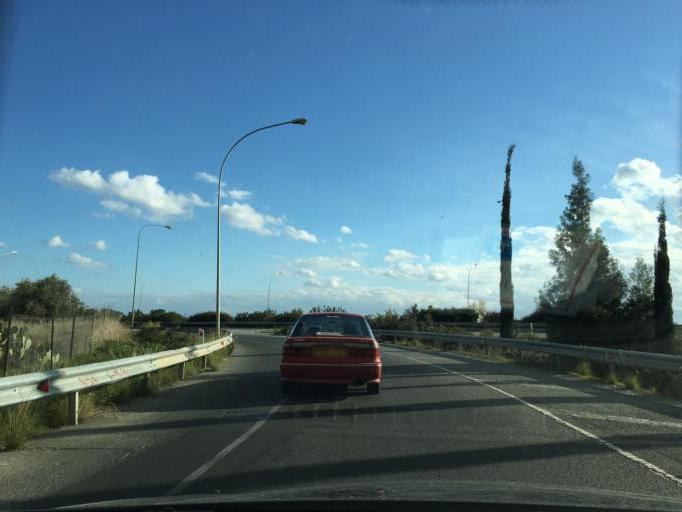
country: CY
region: Limassol
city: Pano Polemidia
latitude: 34.6879
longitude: 32.9920
